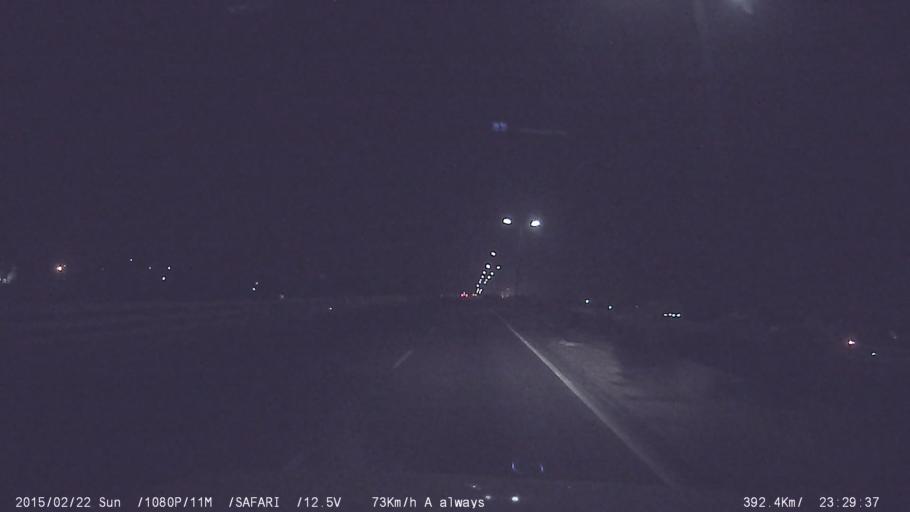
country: IN
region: Tamil Nadu
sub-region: Salem
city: Salem
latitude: 11.6560
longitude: 78.1213
